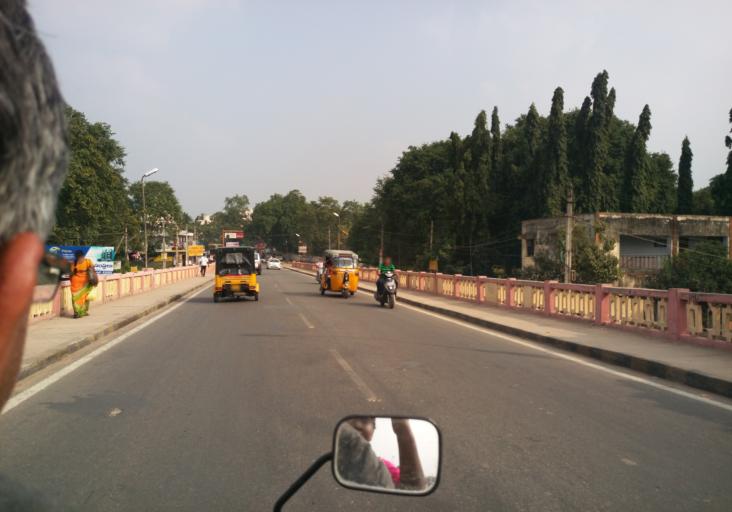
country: IN
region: Andhra Pradesh
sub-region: Chittoor
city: Chittoor
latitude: 13.2166
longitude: 79.1047
